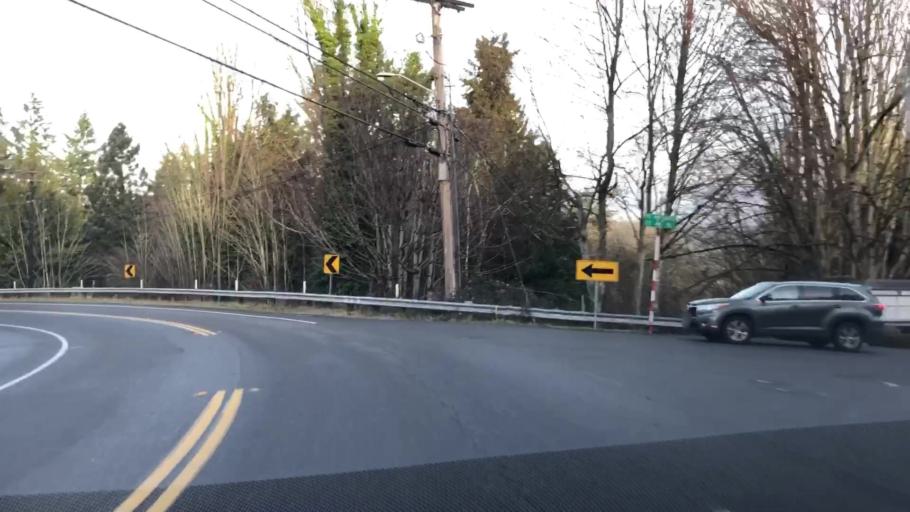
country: US
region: Washington
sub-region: King County
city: West Lake Sammamish
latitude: 47.5666
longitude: -122.1214
